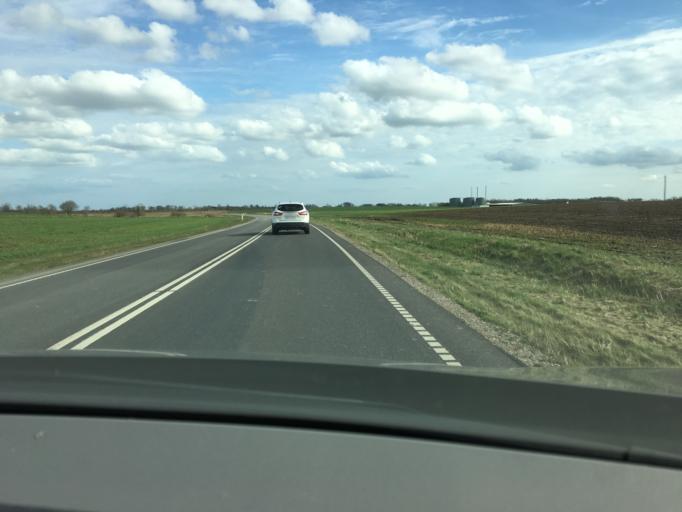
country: DK
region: South Denmark
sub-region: Vejle Kommune
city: Jelling
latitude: 55.7663
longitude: 9.4290
